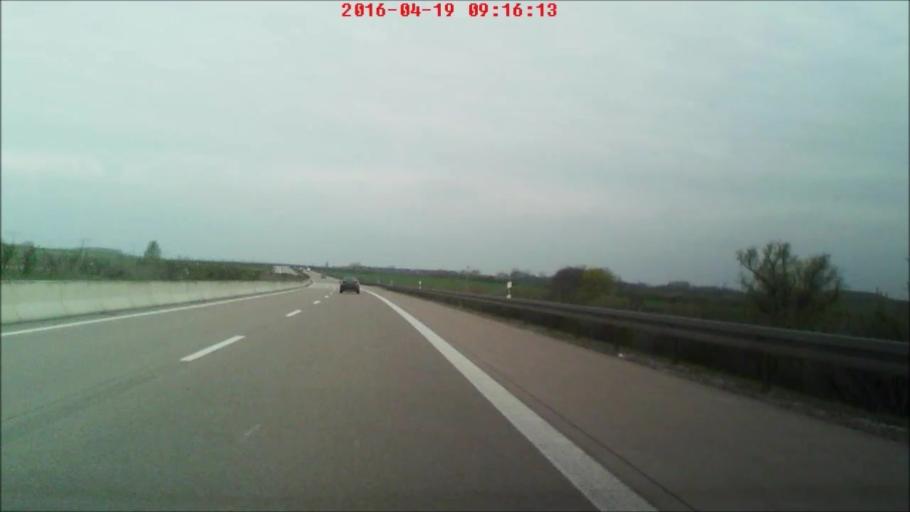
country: DE
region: Thuringia
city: Eckstedt
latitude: 51.0772
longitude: 11.1251
